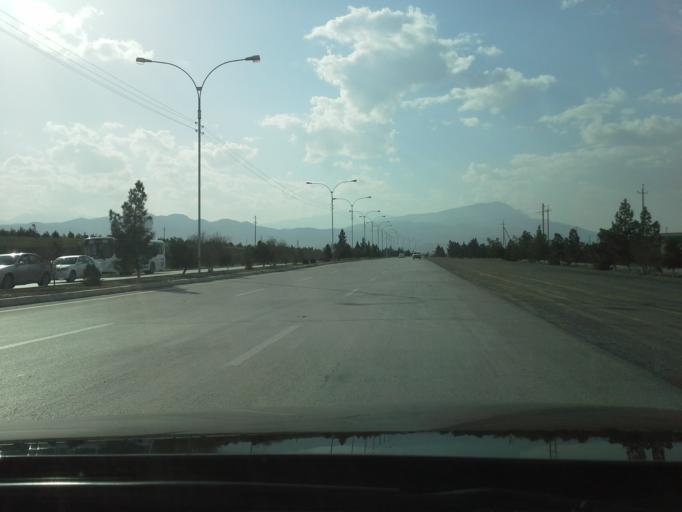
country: TM
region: Ahal
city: Abadan
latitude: 37.9708
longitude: 58.2684
